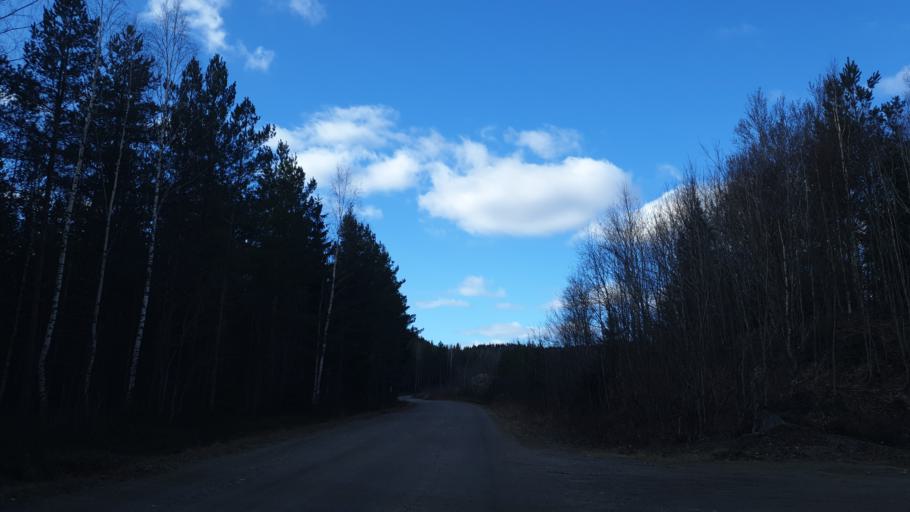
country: SE
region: OErebro
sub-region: Orebro Kommun
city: Garphyttan
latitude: 59.3551
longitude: 14.9809
